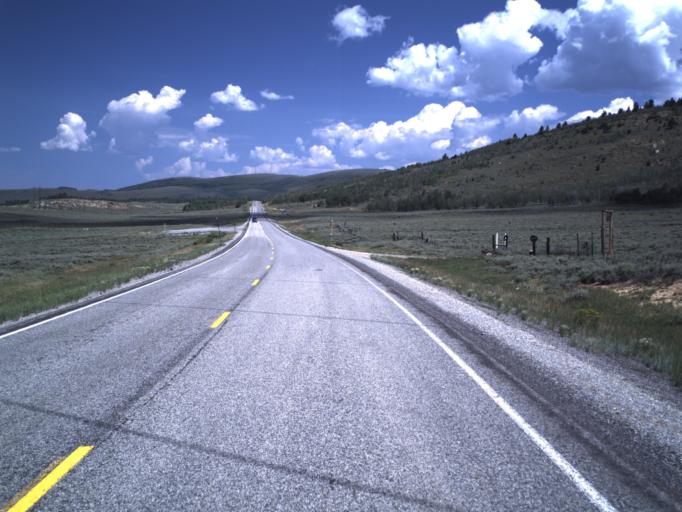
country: US
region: Utah
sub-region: Carbon County
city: Helper
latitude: 39.8374
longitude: -111.1295
